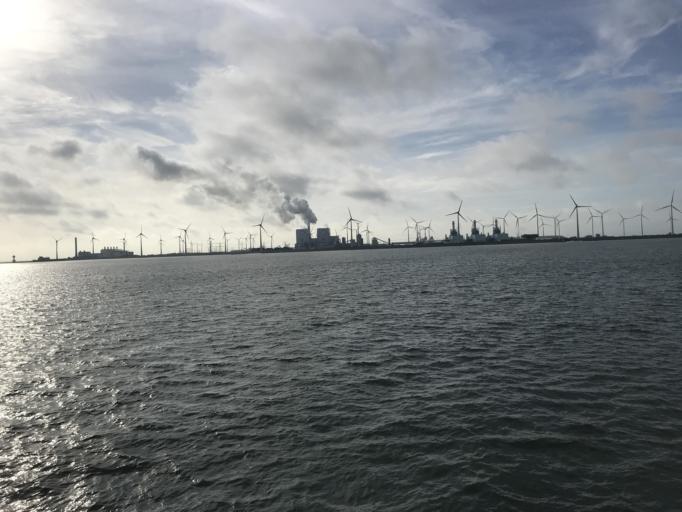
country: NL
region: Groningen
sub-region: Gemeente Appingedam
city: Appingedam
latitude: 53.4668
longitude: 6.8669
